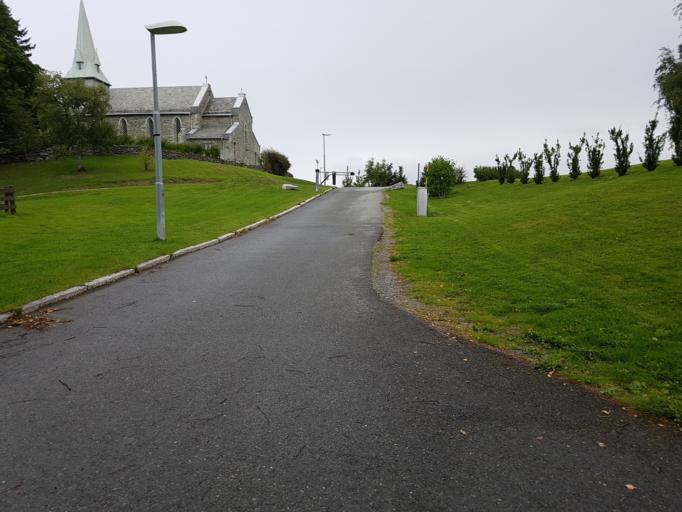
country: NO
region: Sor-Trondelag
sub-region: Trondheim
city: Trondheim
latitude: 63.4041
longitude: 10.3714
